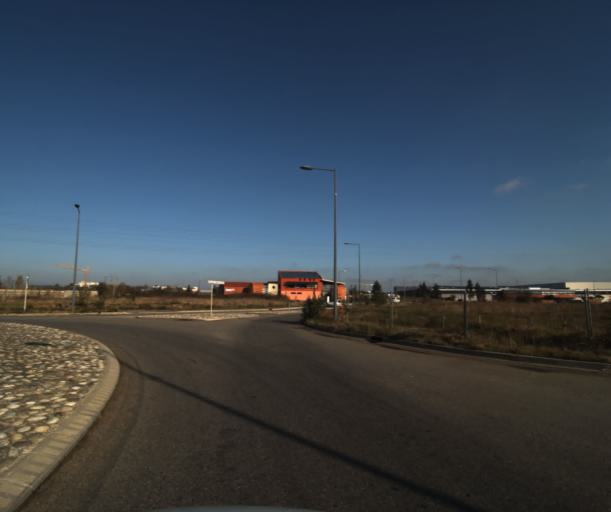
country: FR
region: Midi-Pyrenees
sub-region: Departement de la Haute-Garonne
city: Colomiers
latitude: 43.5998
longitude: 1.3577
